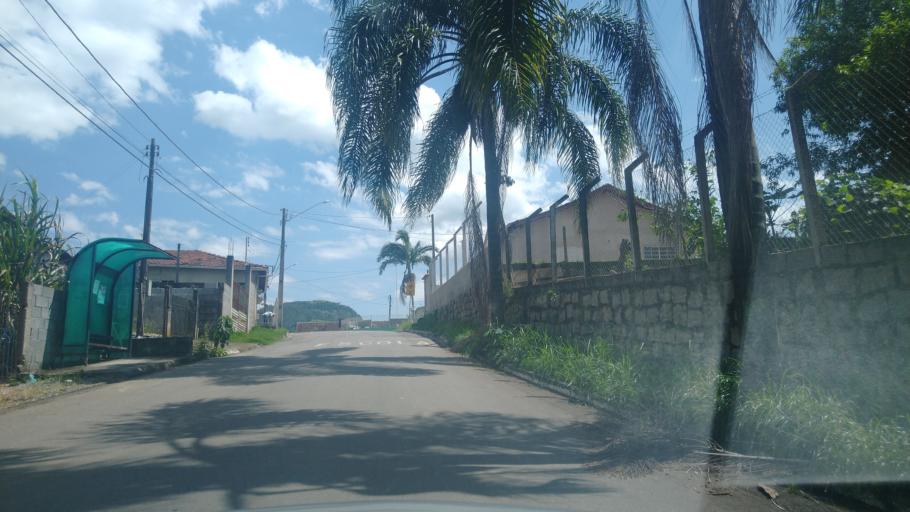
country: BR
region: Minas Gerais
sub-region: Extrema
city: Extrema
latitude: -22.7721
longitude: -46.2858
